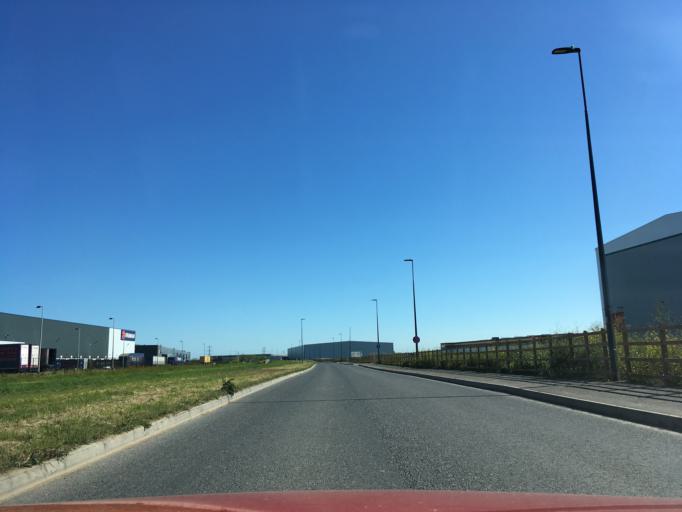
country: GB
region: England
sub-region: South Gloucestershire
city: Severn Beach
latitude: 51.5377
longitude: -2.6503
